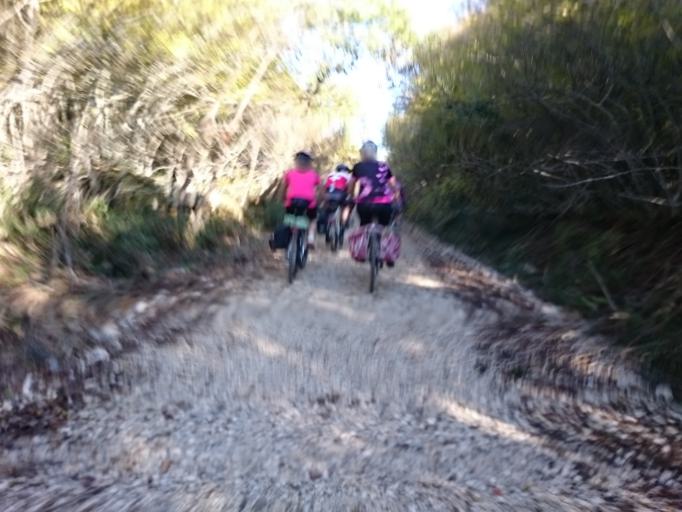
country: HR
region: Istarska
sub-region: Grad Porec
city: Porec
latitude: 45.2388
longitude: 13.6136
